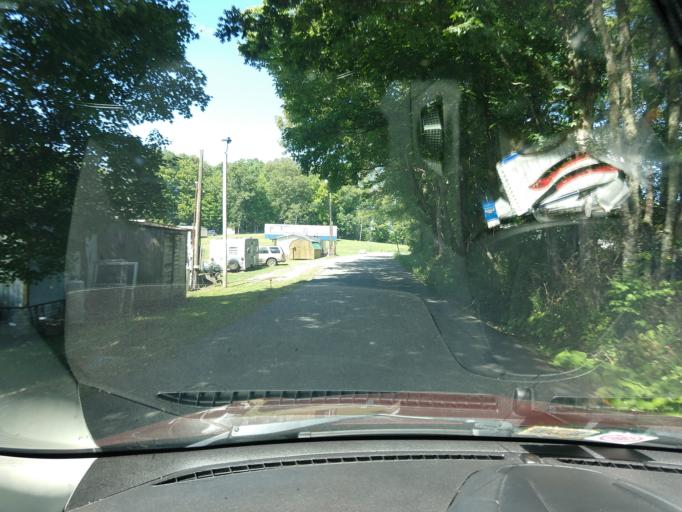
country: US
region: West Virginia
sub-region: Nicholas County
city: Craigsville
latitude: 38.2830
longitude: -80.7455
